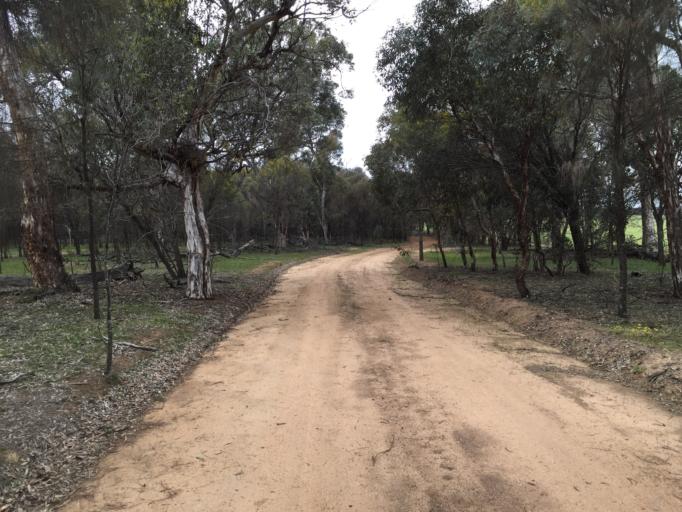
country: AU
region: Western Australia
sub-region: Narrogin
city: Narrogin
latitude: -32.8236
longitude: 116.8889
